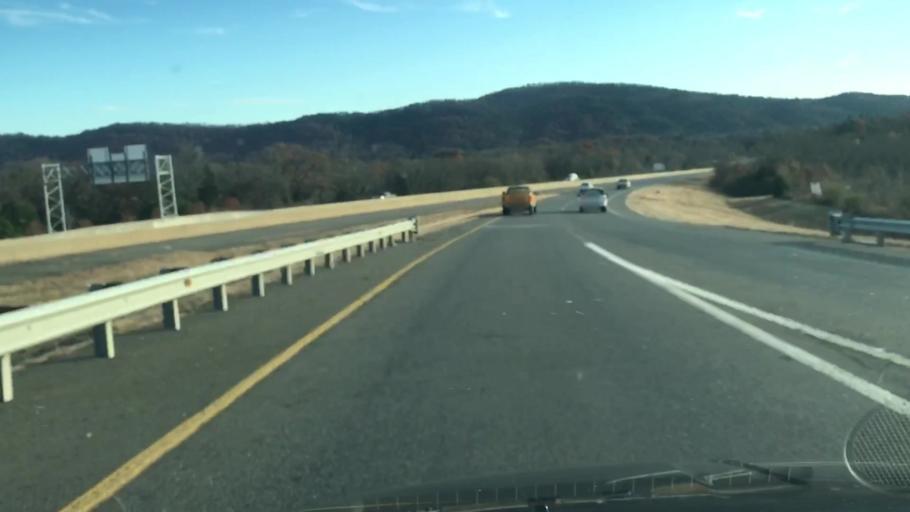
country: US
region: Arkansas
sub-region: Garland County
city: Hot Springs National Park
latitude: 34.5025
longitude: -92.9758
